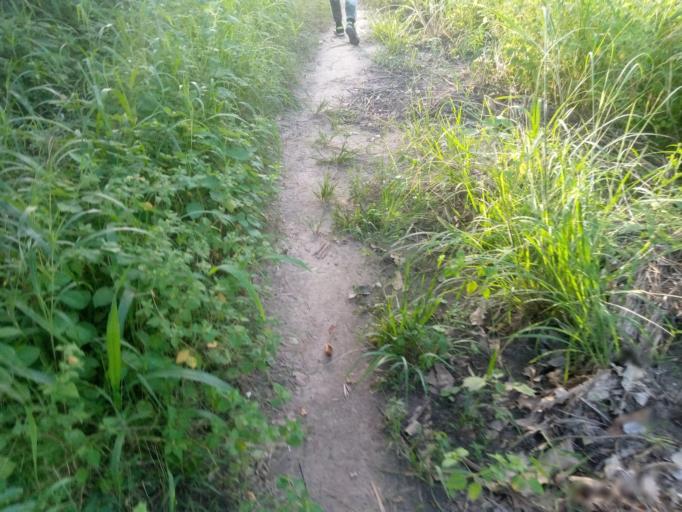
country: GM
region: Western
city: Gunjur
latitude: 13.0363
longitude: -16.7259
